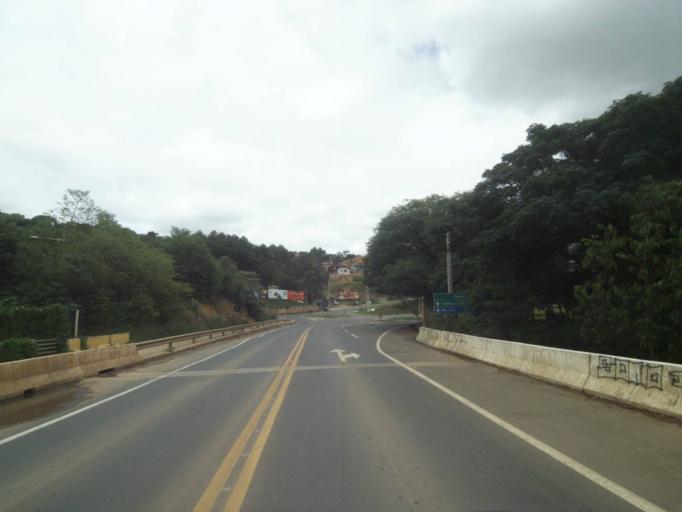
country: BR
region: Parana
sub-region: Telemaco Borba
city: Telemaco Borba
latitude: -24.3129
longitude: -50.6159
